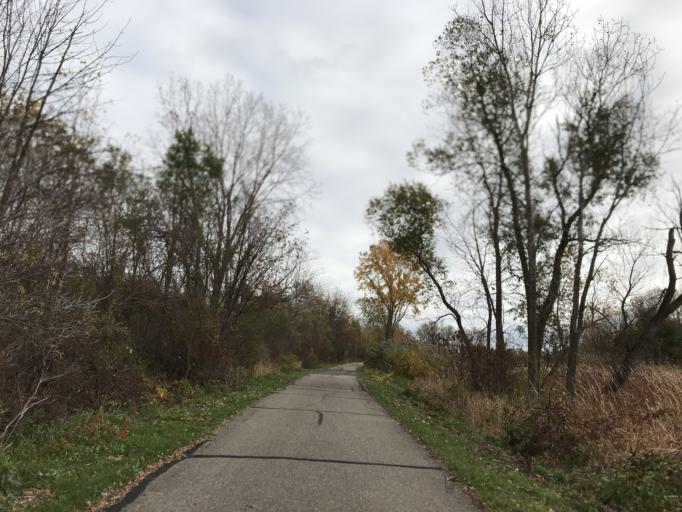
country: US
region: Michigan
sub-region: Oakland County
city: Wixom
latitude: 42.5251
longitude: -83.5951
